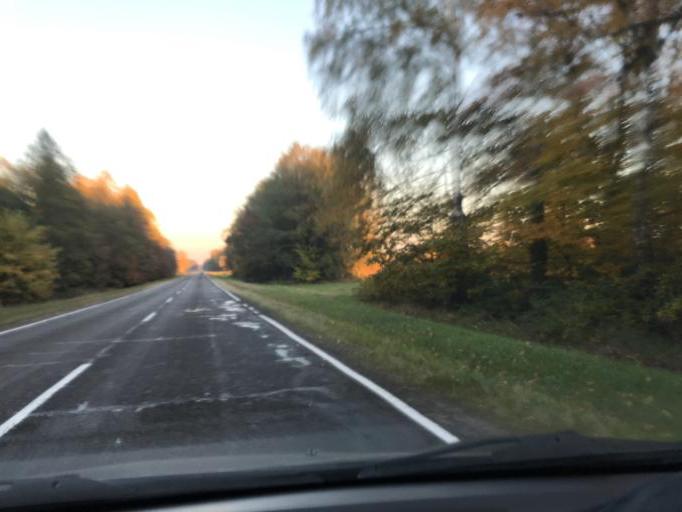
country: BY
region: Mogilev
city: Hlusk
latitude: 53.0683
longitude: 28.5718
